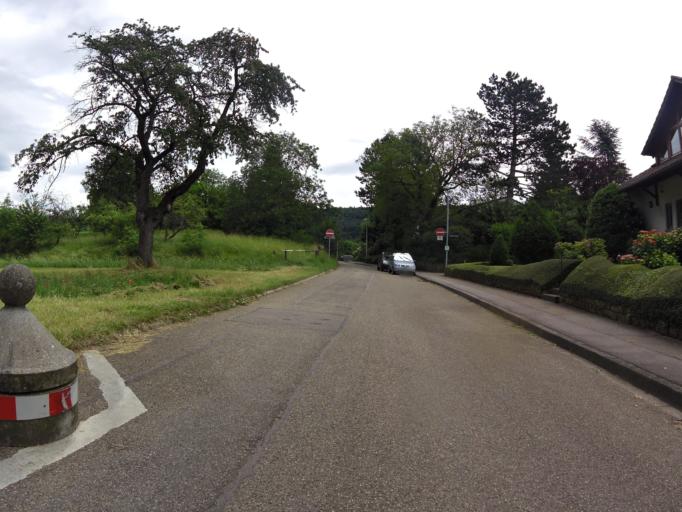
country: DE
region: Baden-Wuerttemberg
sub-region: Freiburg Region
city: Lahr
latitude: 48.3499
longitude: 7.8814
